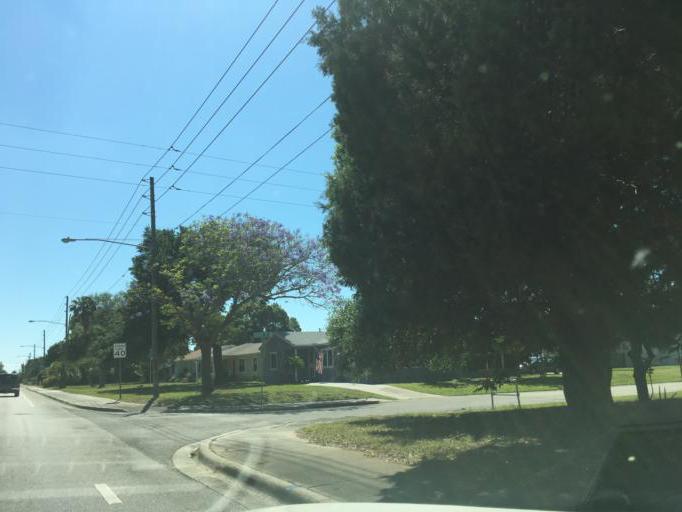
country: US
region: Florida
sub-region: Pinellas County
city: Lealman
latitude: 27.8085
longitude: -82.6291
